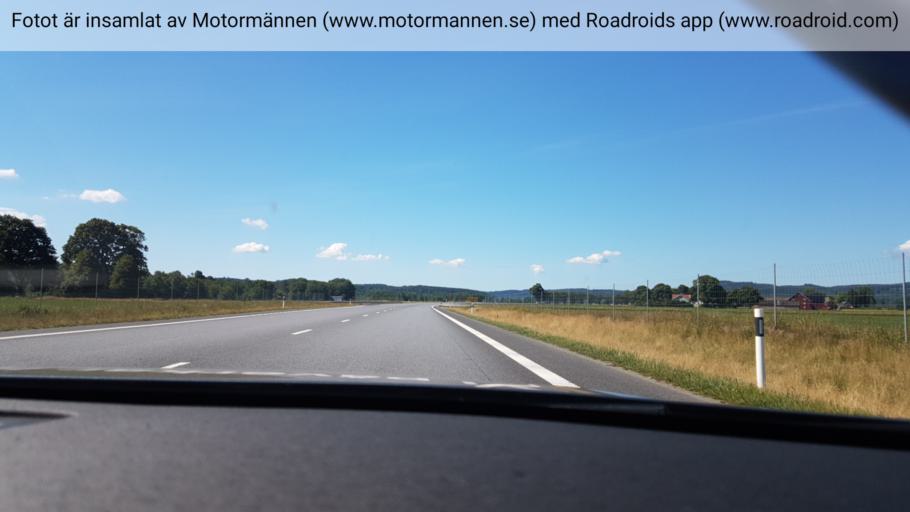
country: SE
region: Vaestra Goetaland
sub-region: Marks Kommun
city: Horred
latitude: 57.4461
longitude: 12.5663
